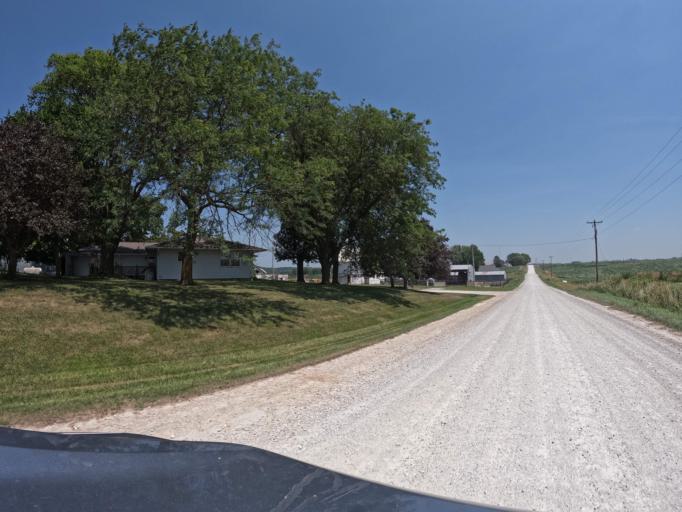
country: US
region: Iowa
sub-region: Keokuk County
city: Sigourney
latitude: 41.2867
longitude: -92.2147
